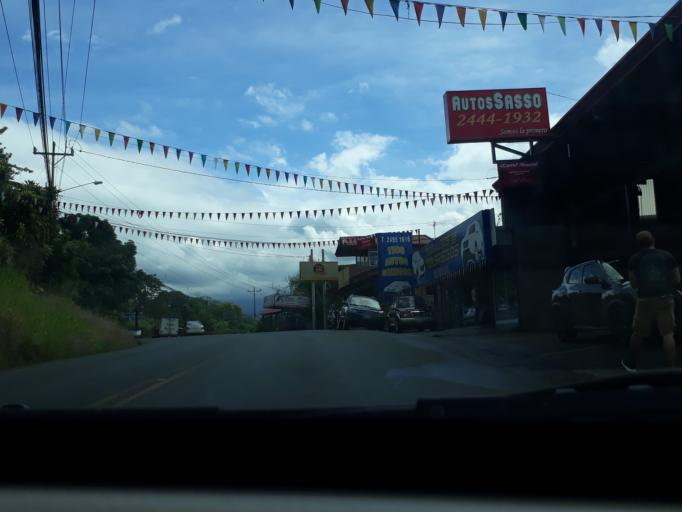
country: CR
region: Alajuela
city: Naranjo
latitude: 10.0411
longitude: -84.3472
